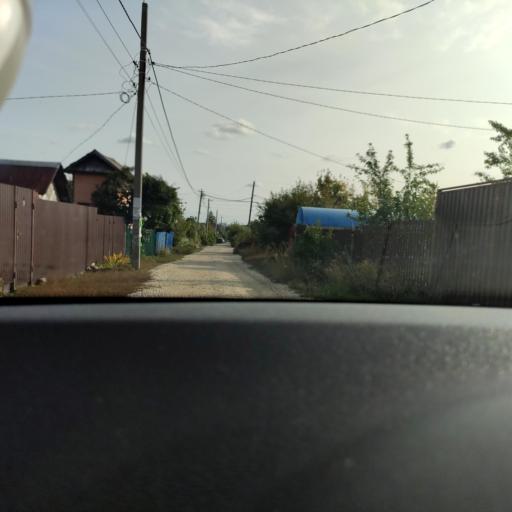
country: RU
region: Samara
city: Petra-Dubrava
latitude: 53.2813
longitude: 50.2957
